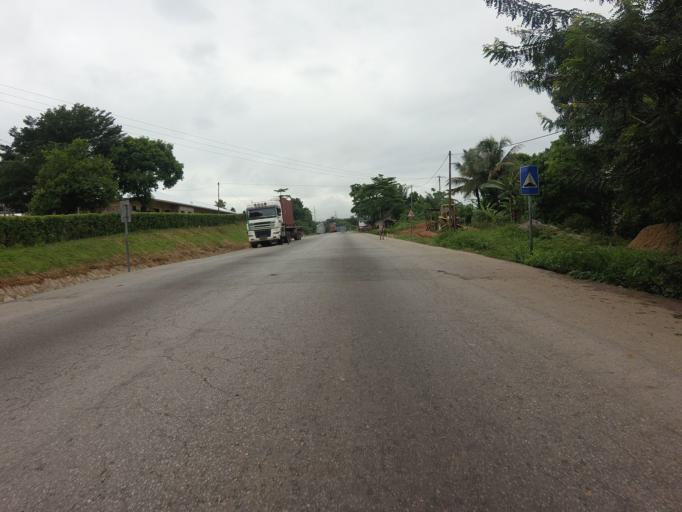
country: GH
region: Eastern
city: Nkawkaw
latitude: 6.4371
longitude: -0.5862
